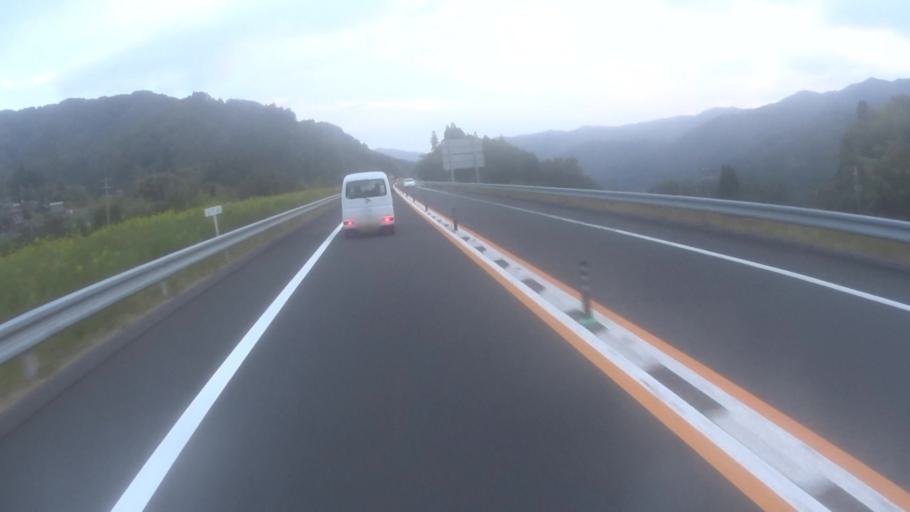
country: JP
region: Kyoto
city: Ayabe
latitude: 35.2926
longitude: 135.3353
